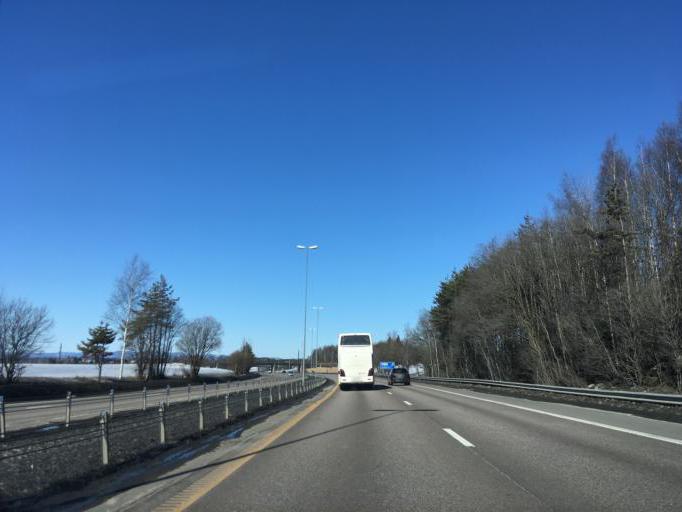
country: NO
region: Akershus
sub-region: Ullensaker
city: Jessheim
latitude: 60.1268
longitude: 11.1651
